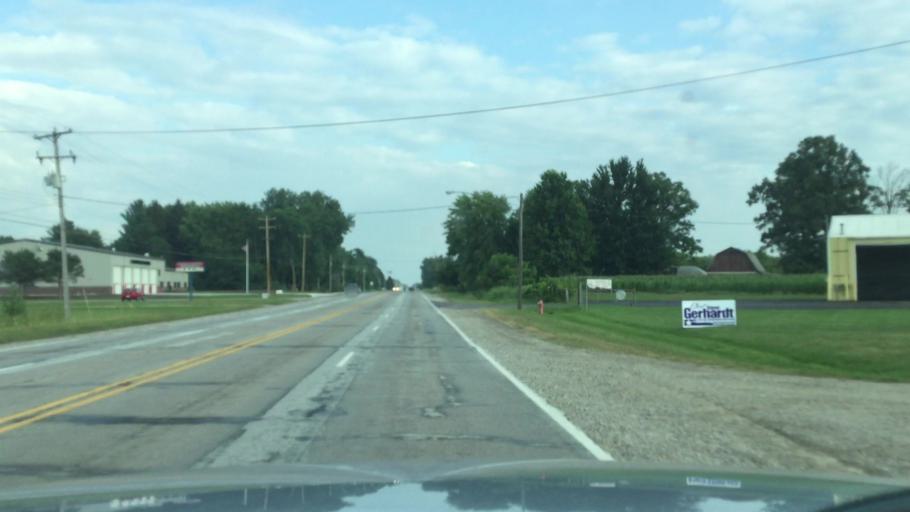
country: US
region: Michigan
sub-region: Saginaw County
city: Birch Run
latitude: 43.2627
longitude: -83.7788
